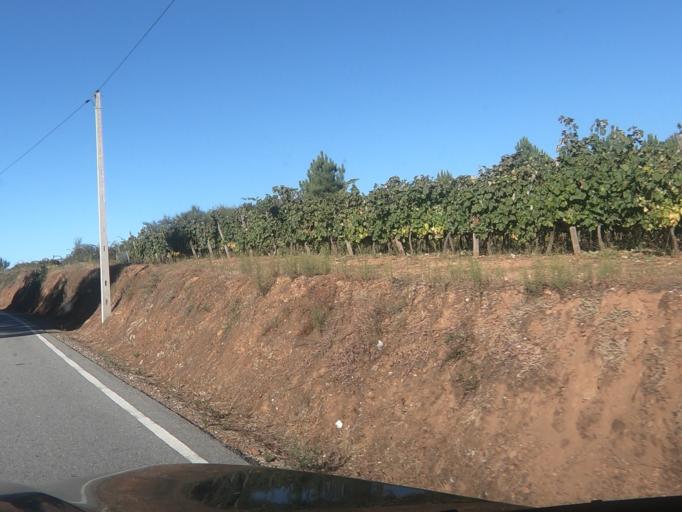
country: PT
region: Vila Real
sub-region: Sabrosa
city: Sabrosa
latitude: 41.2810
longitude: -7.5759
